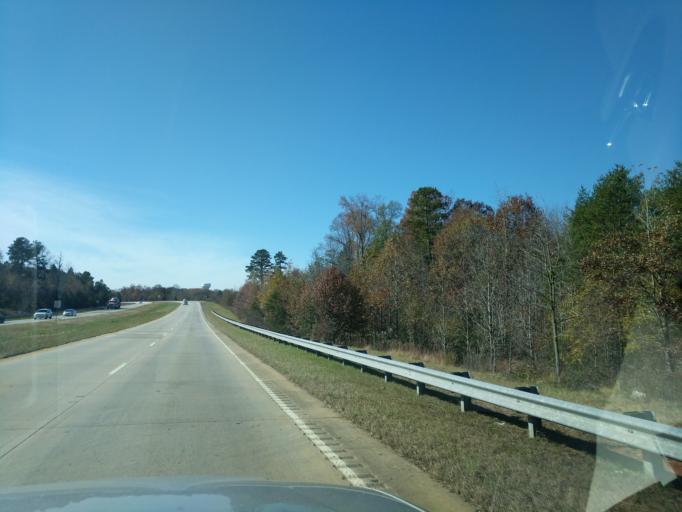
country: US
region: South Carolina
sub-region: Greenville County
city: Greer
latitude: 34.9112
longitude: -82.2135
